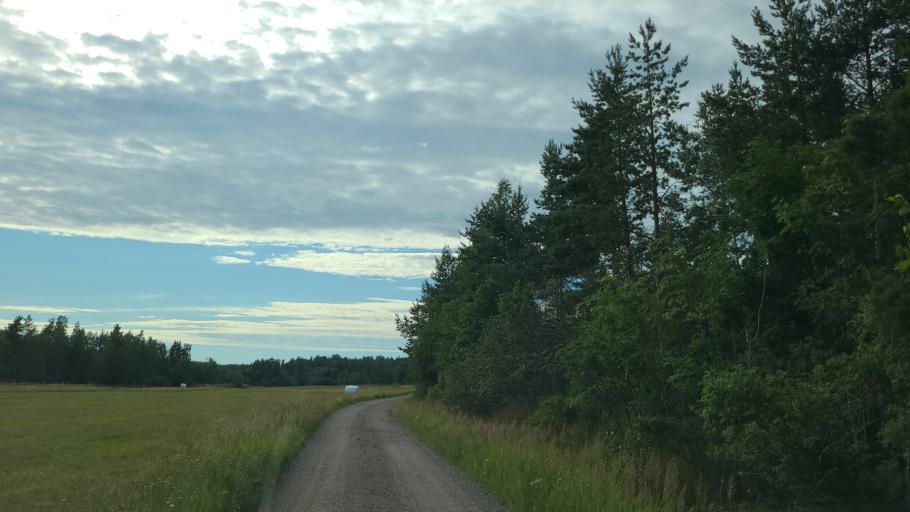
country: FI
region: Varsinais-Suomi
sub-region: Aboland-Turunmaa
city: Nagu
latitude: 60.2815
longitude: 21.9420
